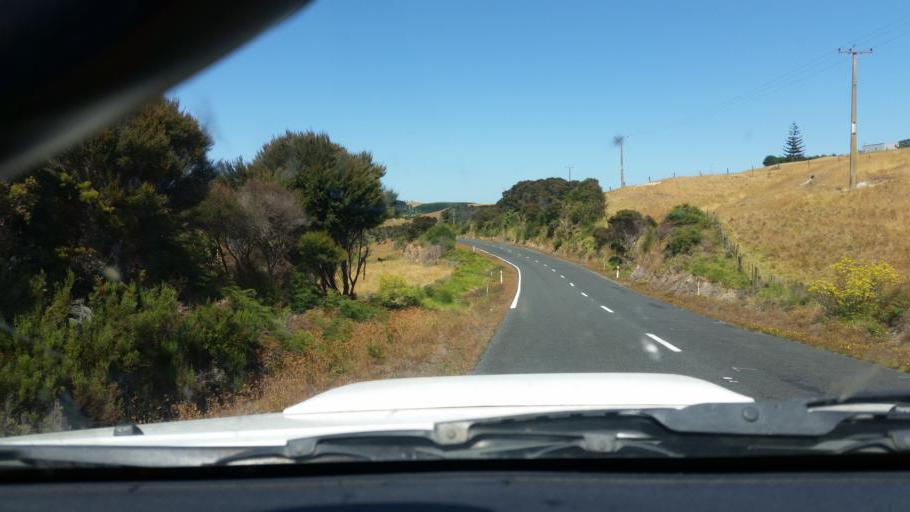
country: NZ
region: Northland
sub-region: Kaipara District
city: Dargaville
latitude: -35.8275
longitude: 173.6721
